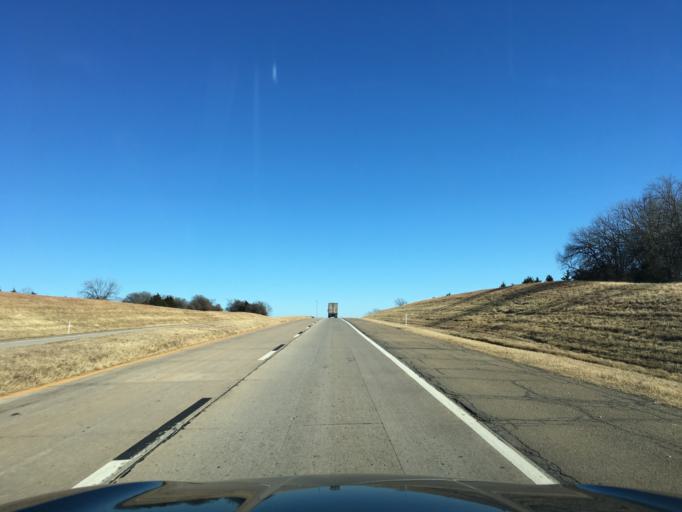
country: US
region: Oklahoma
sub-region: Pawnee County
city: Pawnee
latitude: 36.2248
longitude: -96.7750
